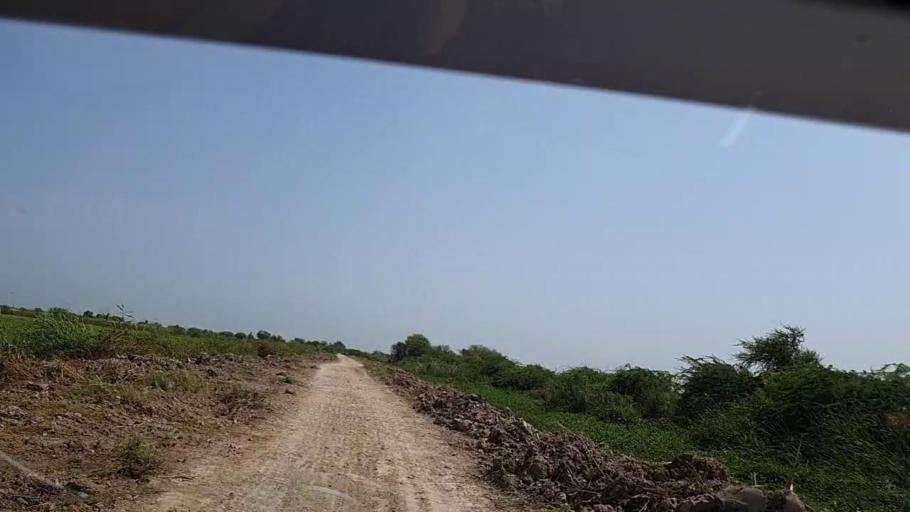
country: PK
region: Sindh
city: Rajo Khanani
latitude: 24.9373
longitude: 68.8750
